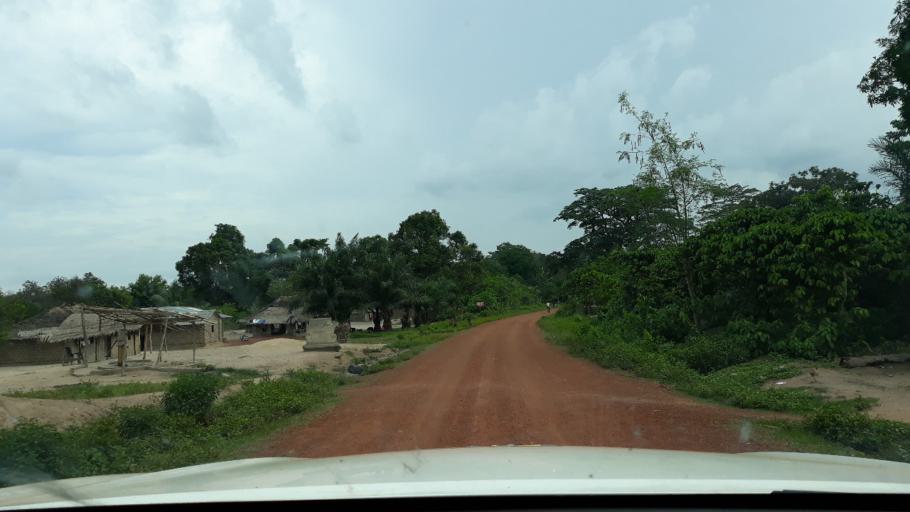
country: CD
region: Equateur
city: Libenge
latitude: 3.7059
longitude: 18.7684
